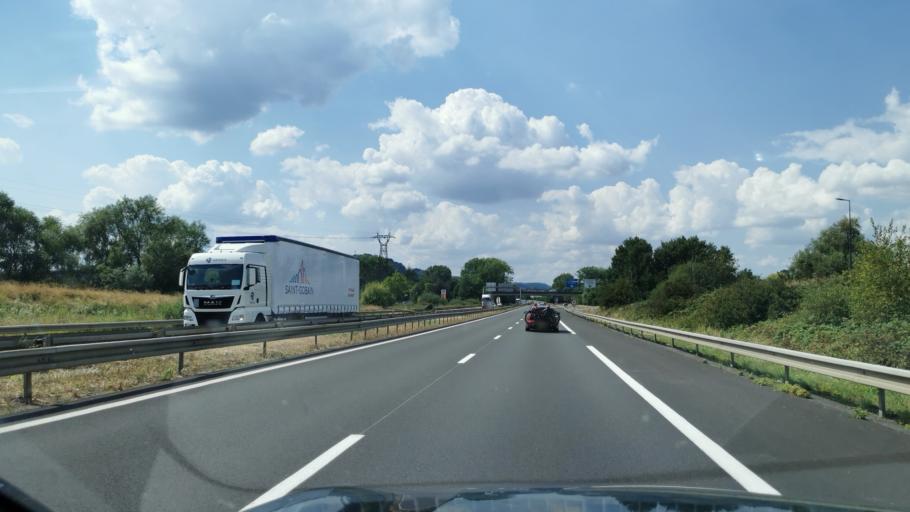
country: FR
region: Lorraine
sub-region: Departement de la Moselle
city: Fameck
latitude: 49.3072
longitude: 6.1227
